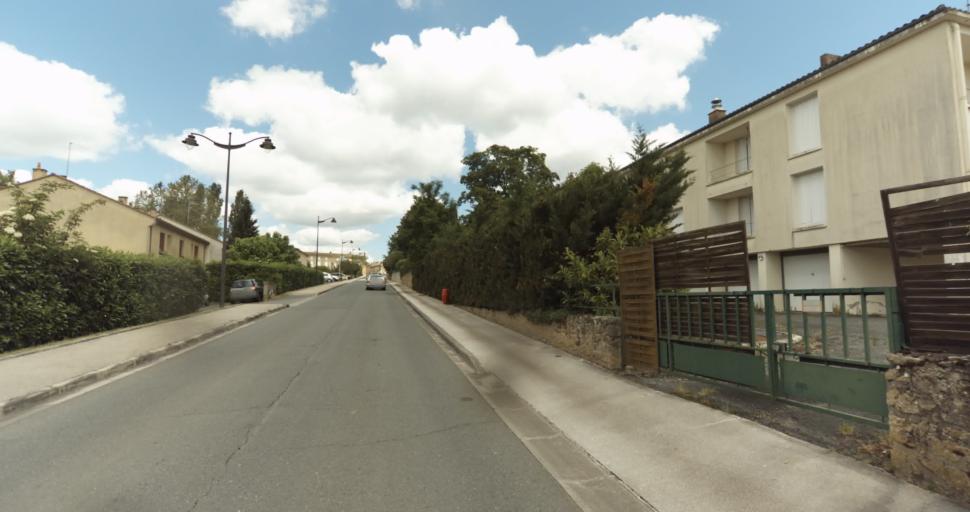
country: FR
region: Aquitaine
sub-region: Departement de la Dordogne
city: Beaumont-du-Perigord
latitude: 44.7647
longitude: 0.7667
